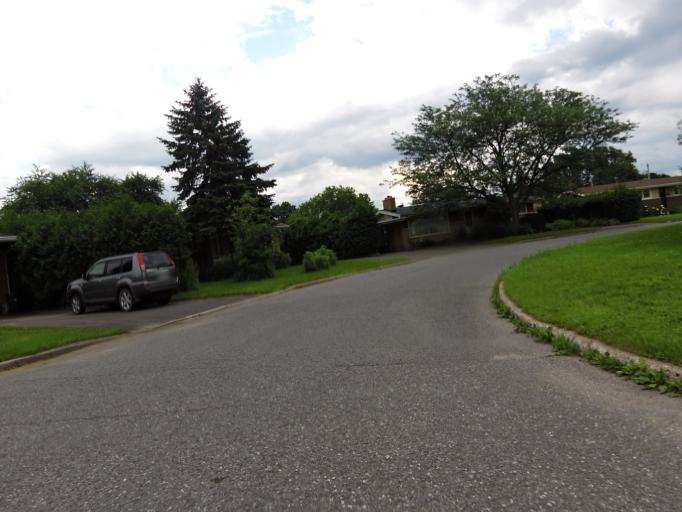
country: CA
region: Ontario
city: Ottawa
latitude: 45.3431
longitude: -75.7344
